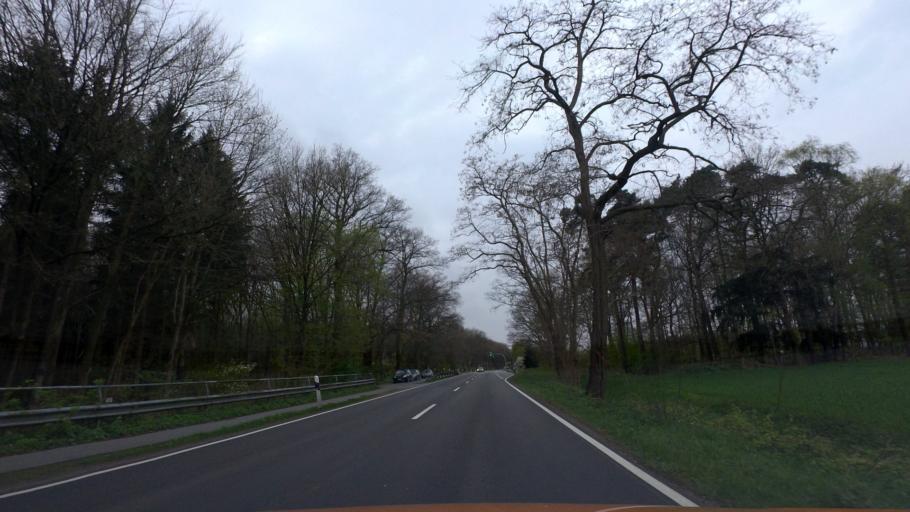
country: DE
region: Lower Saxony
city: Vechta
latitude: 52.7260
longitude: 8.2405
